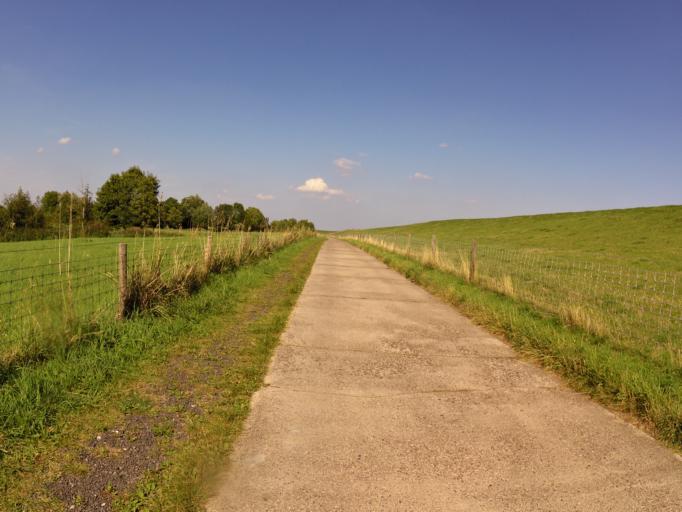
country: DE
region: Lower Saxony
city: Nordenham
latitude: 53.4096
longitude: 8.4685
